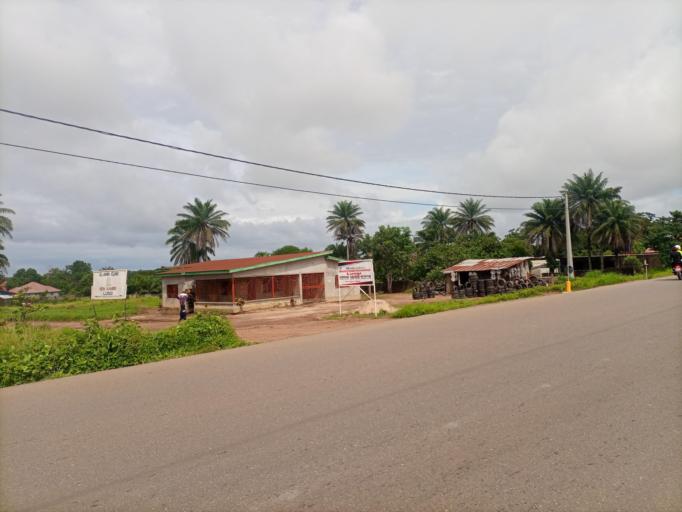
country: SL
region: Northern Province
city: Masoyila
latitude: 8.6003
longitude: -13.1754
